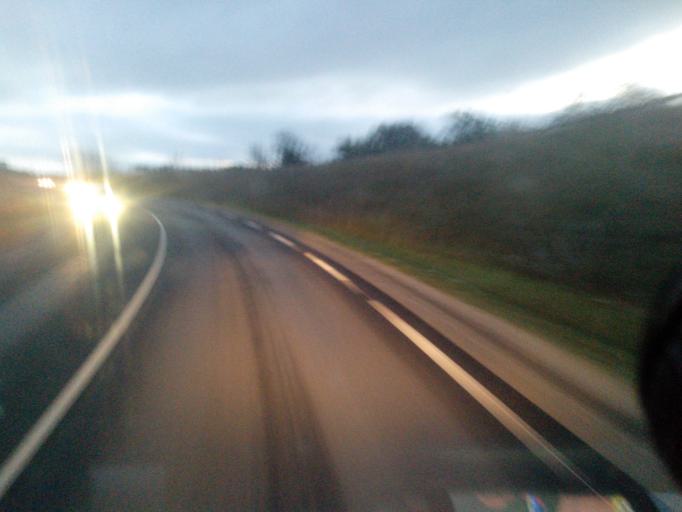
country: FR
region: Languedoc-Roussillon
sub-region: Departement de l'Herault
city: Nebian
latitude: 43.6430
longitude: 3.4458
